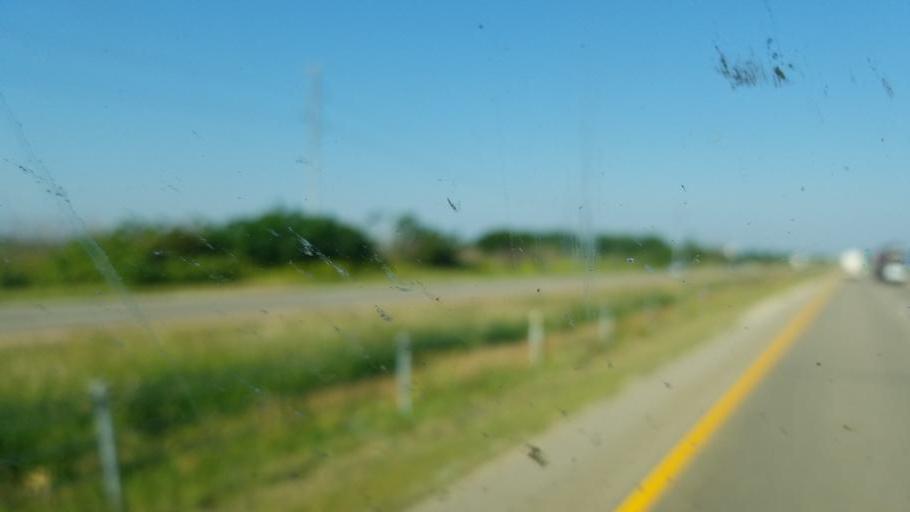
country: US
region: Illinois
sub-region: LaSalle County
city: Deer Park
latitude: 41.3679
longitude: -88.9755
